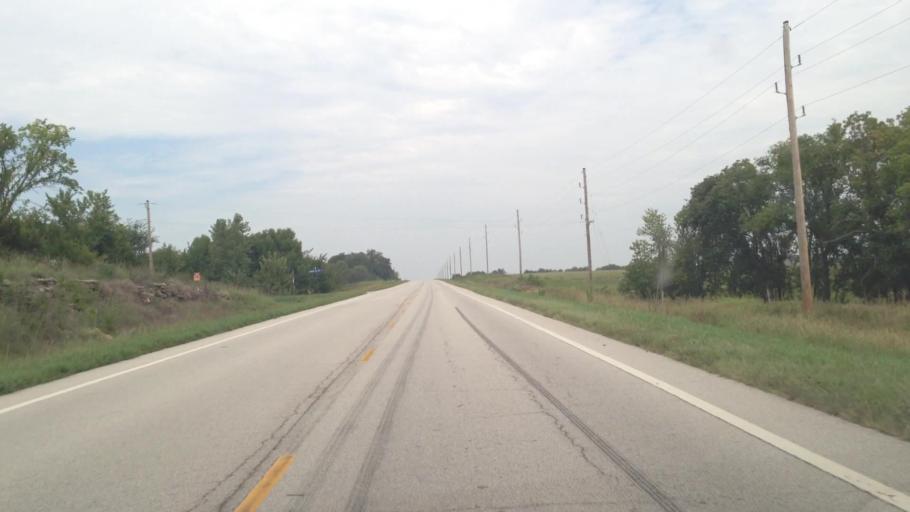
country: US
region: Kansas
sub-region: Allen County
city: Iola
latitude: 37.9642
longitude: -95.1701
